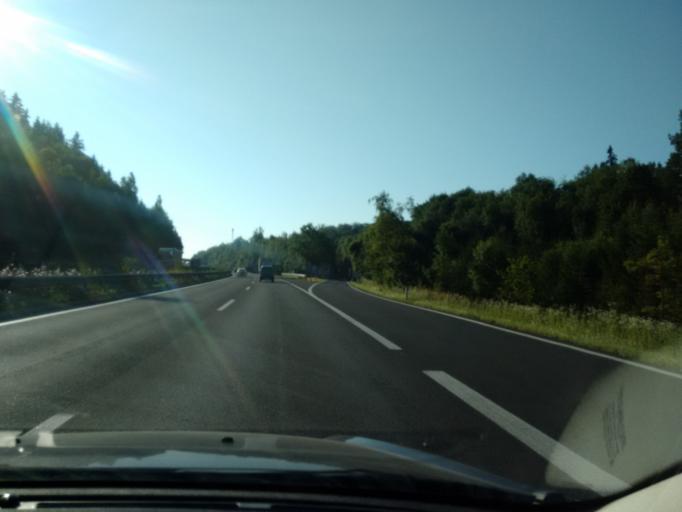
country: AT
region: Upper Austria
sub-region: Wels-Land
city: Gunskirchen
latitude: 48.1859
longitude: 13.9617
